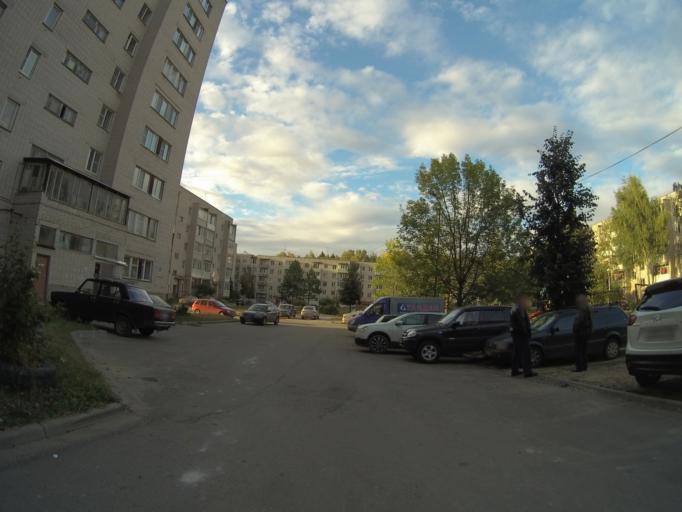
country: RU
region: Vladimir
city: Vladimir
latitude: 56.1104
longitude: 40.2791
